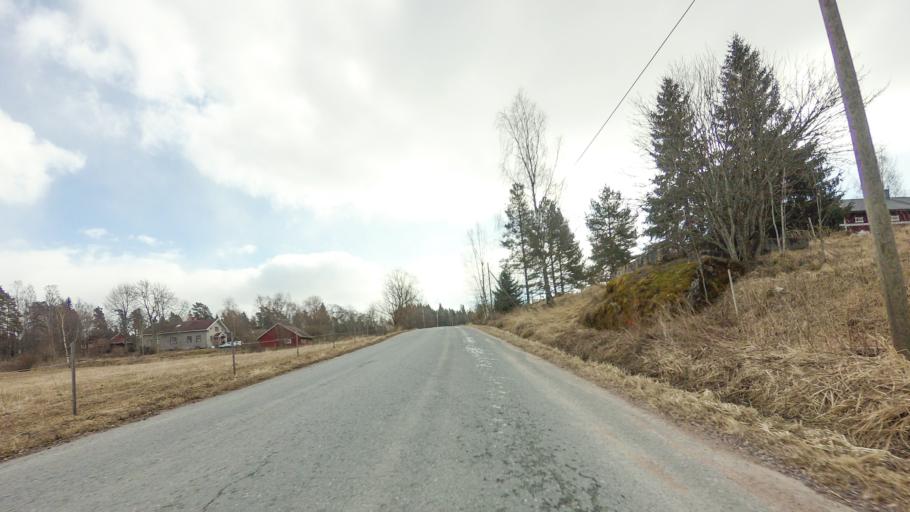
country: FI
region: Varsinais-Suomi
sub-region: Salo
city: Suomusjaervi
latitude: 60.3167
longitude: 23.7107
